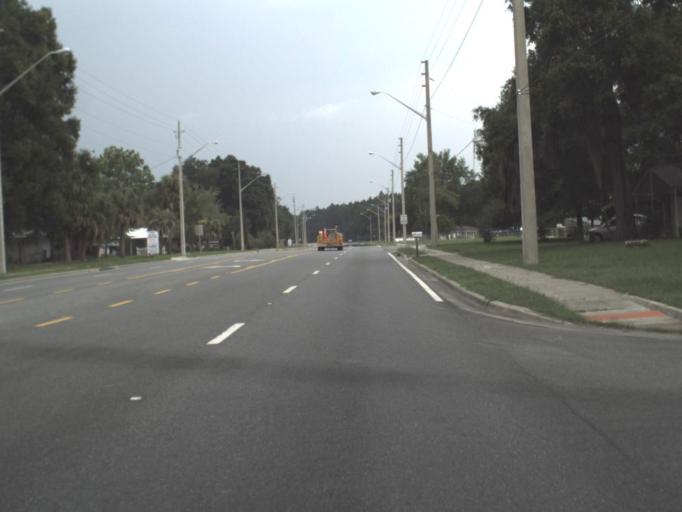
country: US
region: Florida
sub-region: Levy County
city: Chiefland
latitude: 29.4821
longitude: -82.8548
